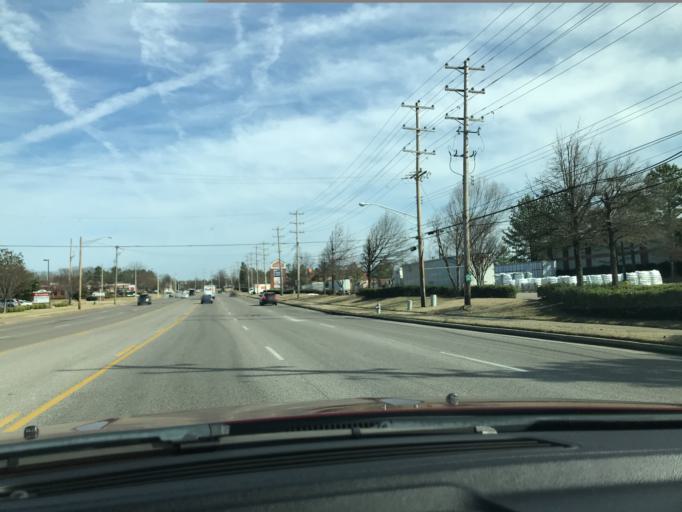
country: US
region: Tennessee
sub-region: Shelby County
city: Germantown
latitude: 35.0489
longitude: -89.8016
